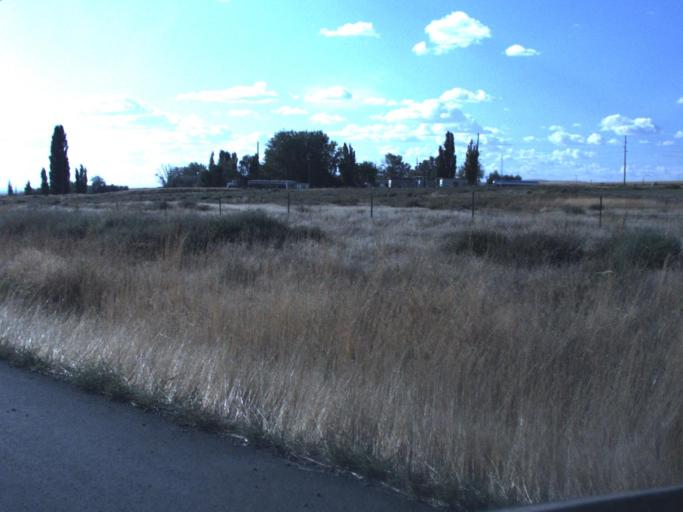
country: US
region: Oregon
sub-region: Morrow County
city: Irrigon
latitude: 45.9514
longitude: -119.4300
